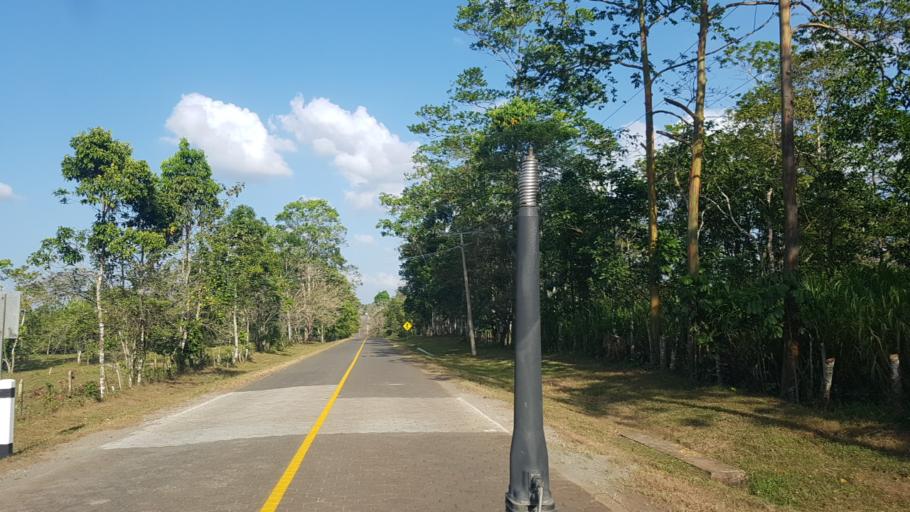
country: NI
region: Atlantico Sur
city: Nueva Guinea
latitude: 11.6901
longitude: -84.4234
